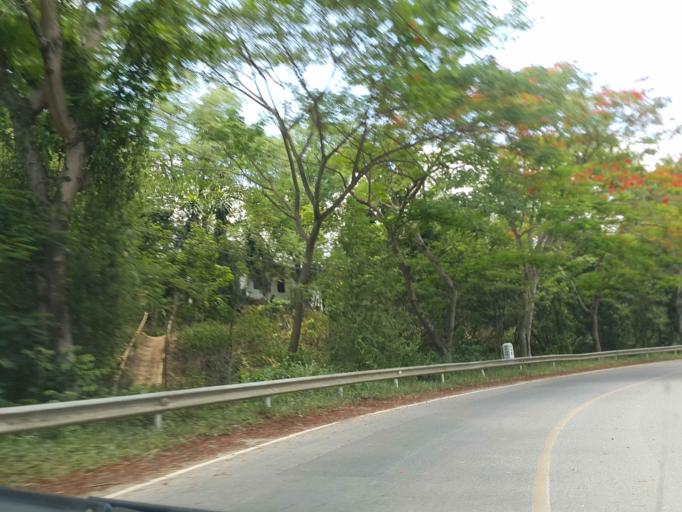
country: TH
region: Chiang Mai
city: Hang Dong
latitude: 18.7429
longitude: 98.8895
